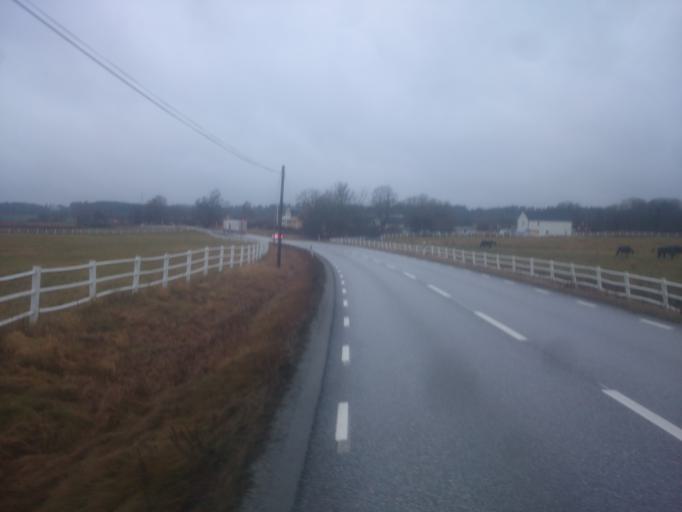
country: SE
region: Uppsala
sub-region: Habo Kommun
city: Balsta
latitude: 59.6439
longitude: 17.6103
